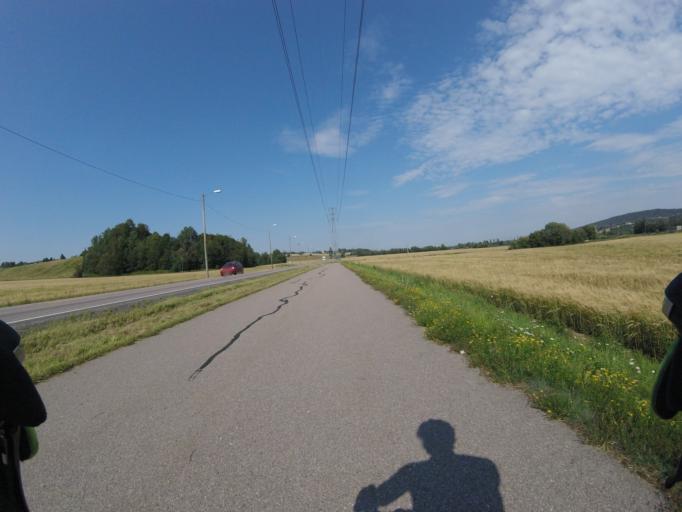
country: NO
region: Akershus
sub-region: Skedsmo
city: Leirsund
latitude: 59.9833
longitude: 11.0696
